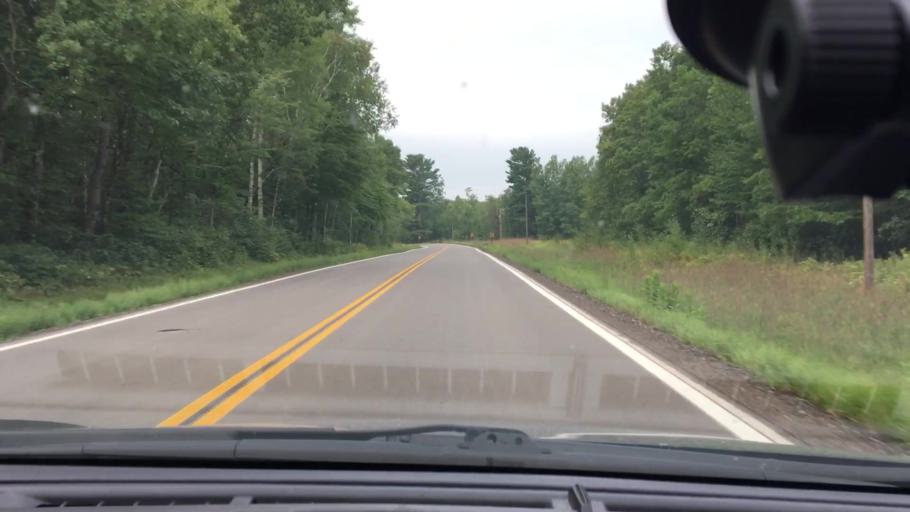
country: US
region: Minnesota
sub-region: Crow Wing County
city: Cross Lake
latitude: 46.6622
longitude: -93.9594
